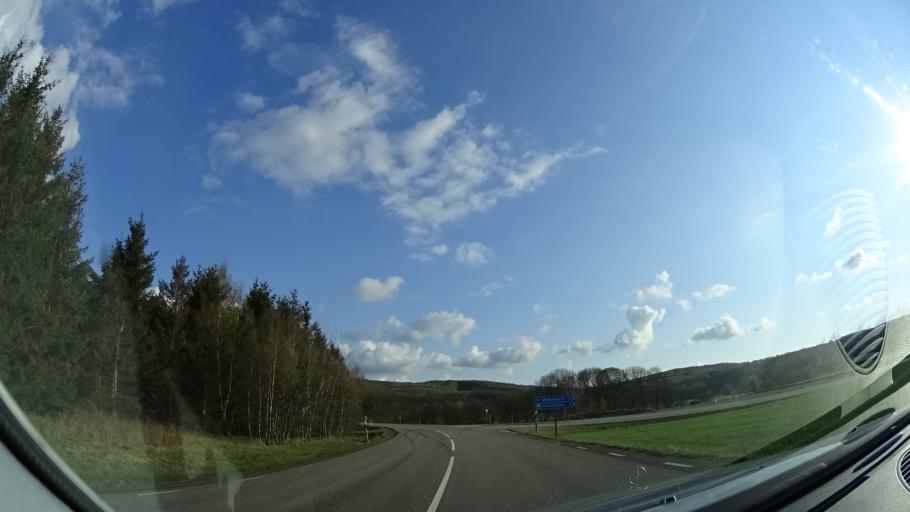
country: SE
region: Skane
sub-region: Klippans Kommun
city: Ljungbyhed
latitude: 56.0533
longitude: 13.2401
